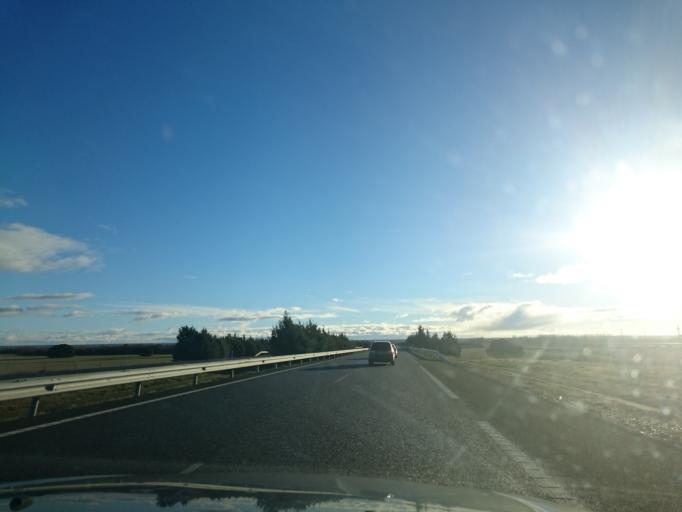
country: ES
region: Castille and Leon
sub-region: Provincia de Leon
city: Bercianos del Real Camino
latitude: 42.3911
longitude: -5.1268
